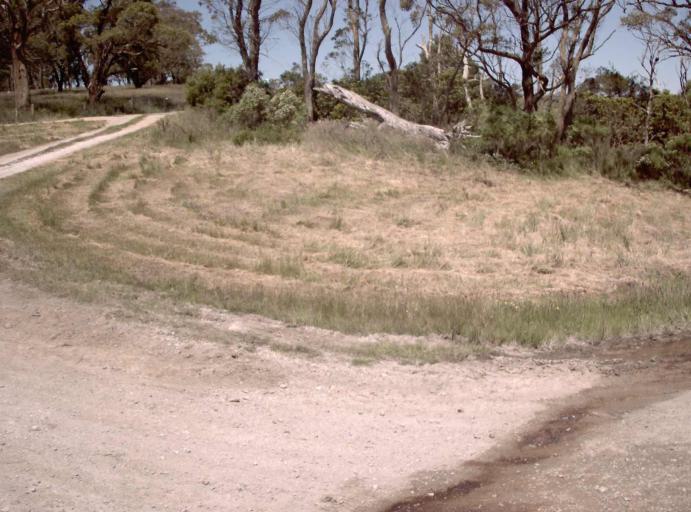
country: AU
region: Victoria
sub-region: Bass Coast
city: North Wonthaggi
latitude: -38.7469
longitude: 146.0747
